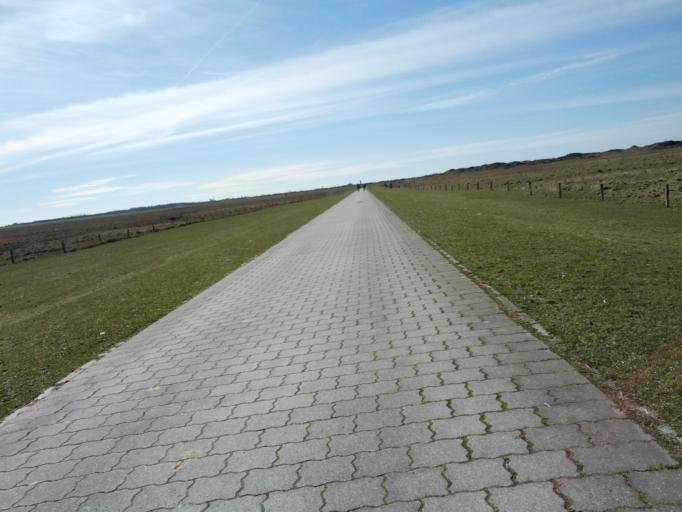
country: DE
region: Lower Saxony
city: Langeoog
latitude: 53.7496
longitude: 7.5279
